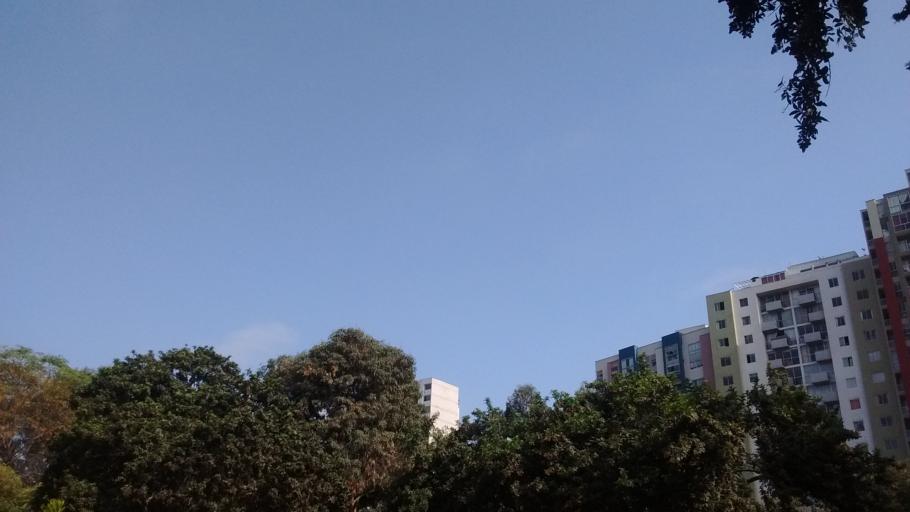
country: PE
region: Lima
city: Lima
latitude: -12.0690
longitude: -77.0440
